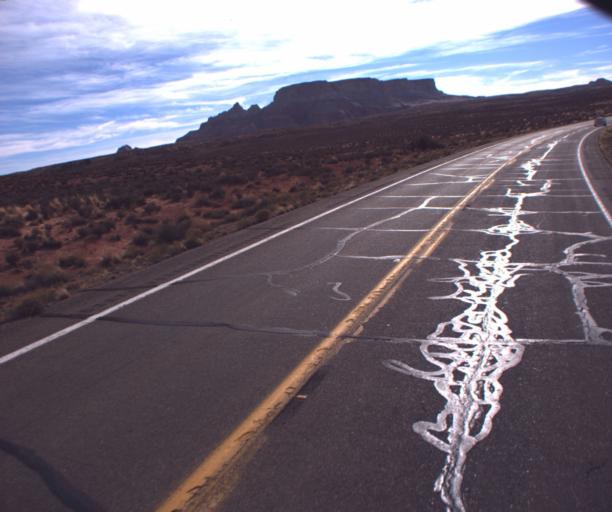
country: US
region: Arizona
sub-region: Coconino County
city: LeChee
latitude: 36.8787
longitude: -111.3451
